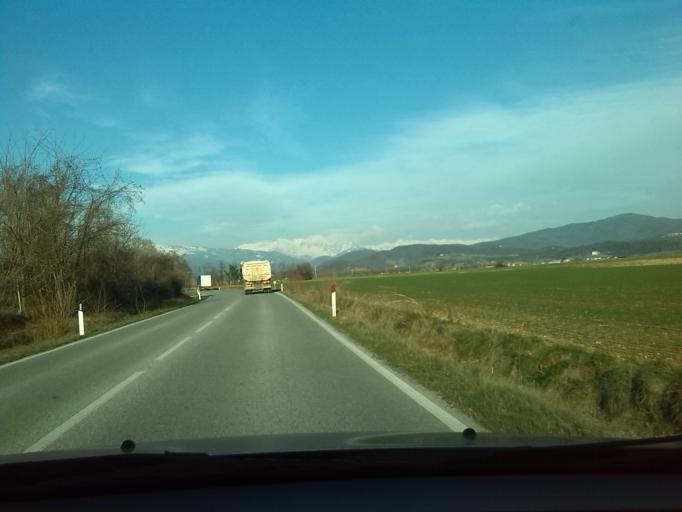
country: IT
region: Friuli Venezia Giulia
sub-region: Provincia di Udine
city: Premariacco
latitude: 46.0561
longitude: 13.4133
